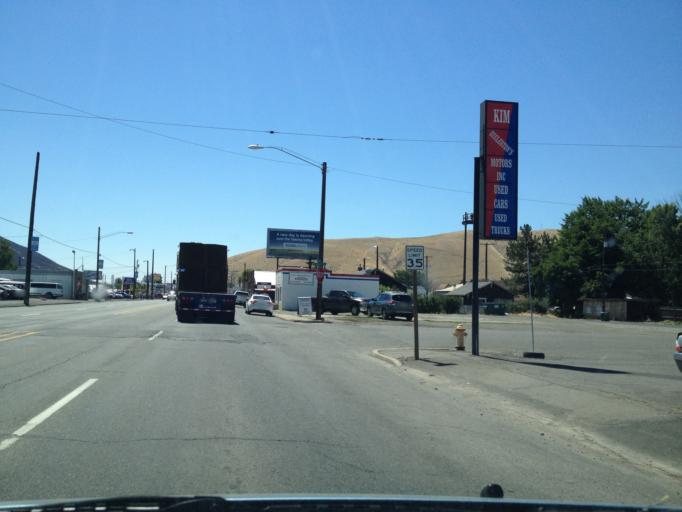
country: US
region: Washington
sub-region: Yakima County
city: Union Gap
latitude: 46.5512
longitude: -120.4754
